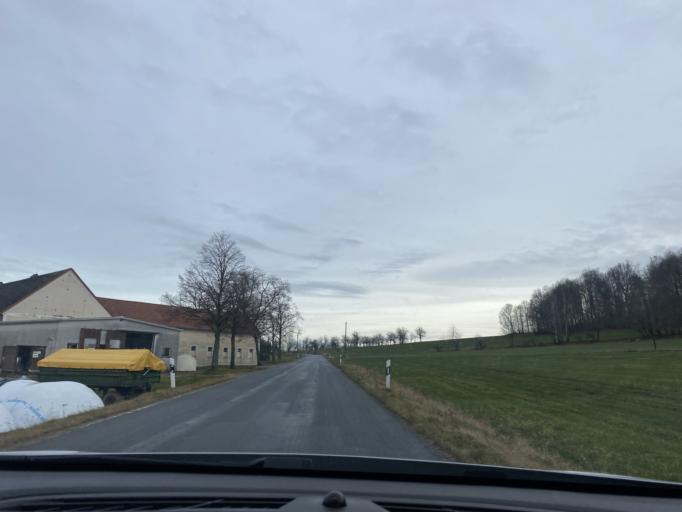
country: DE
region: Saxony
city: Schonau-Berzdorf
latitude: 51.0981
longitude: 14.8981
